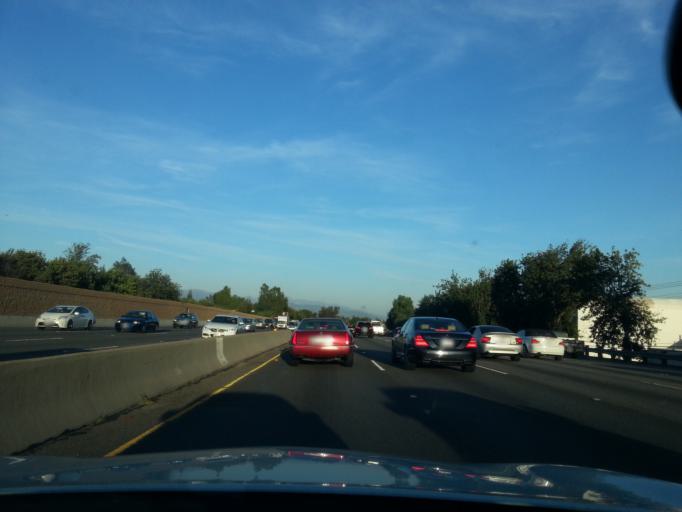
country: US
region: California
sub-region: Los Angeles County
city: Woodland Hills
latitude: 34.1734
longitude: -118.5618
